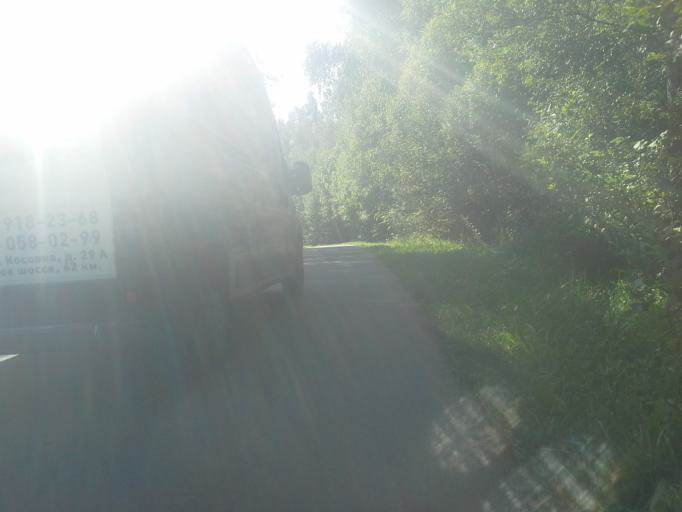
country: RU
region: Moskovskaya
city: Kievskij
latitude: 55.3331
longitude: 36.9955
